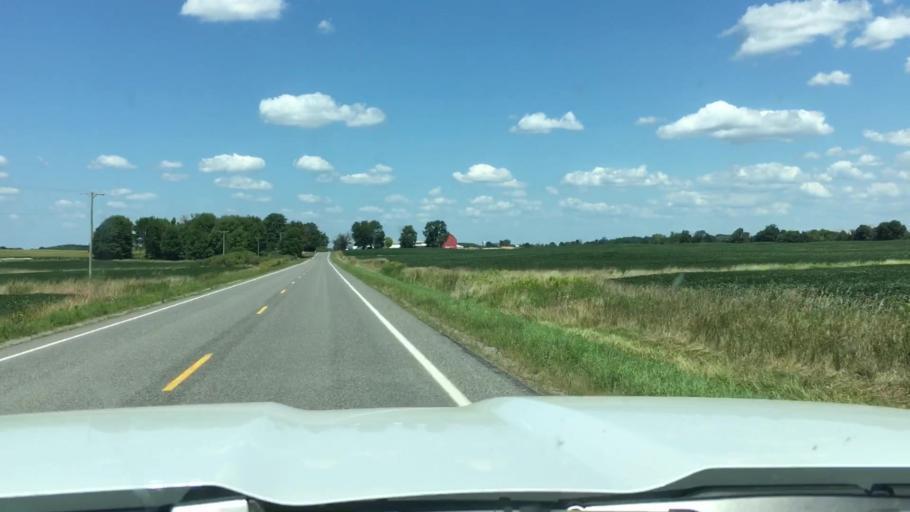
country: US
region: Michigan
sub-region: Muskegon County
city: Ravenna
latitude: 43.1661
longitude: -85.9877
